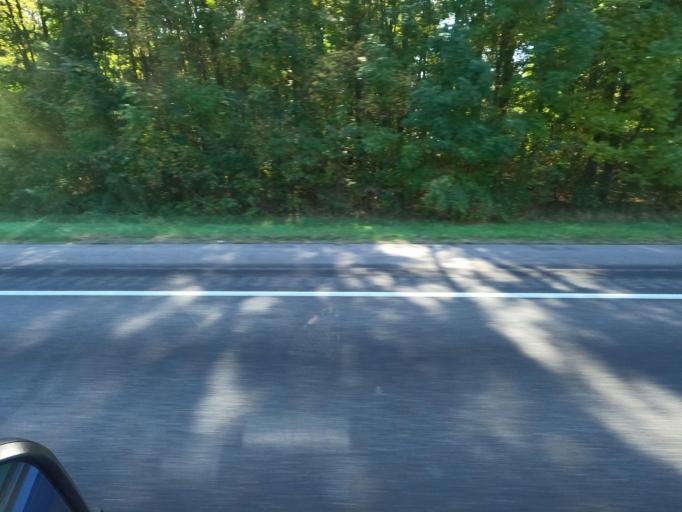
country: US
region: Tennessee
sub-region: Tipton County
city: Mason
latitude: 35.3762
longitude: -89.4543
